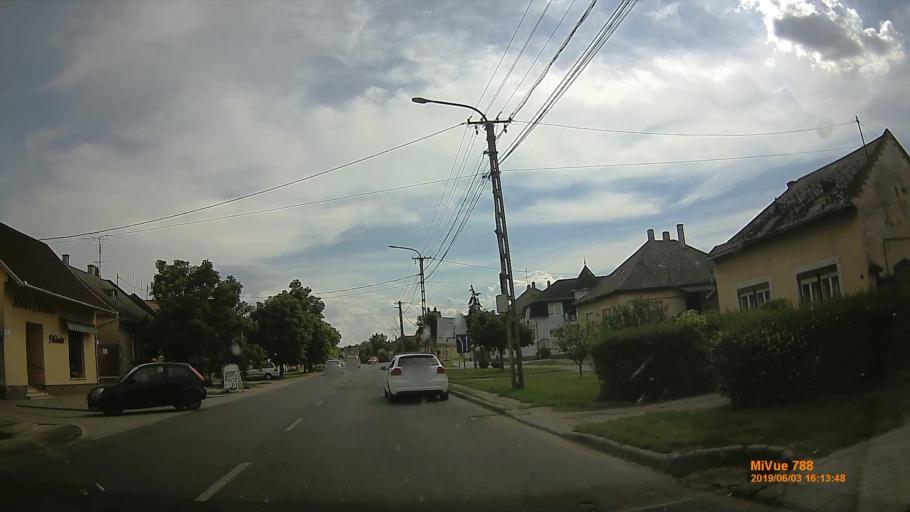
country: HU
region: Tolna
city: Dunafoldvar
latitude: 46.8041
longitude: 18.9221
